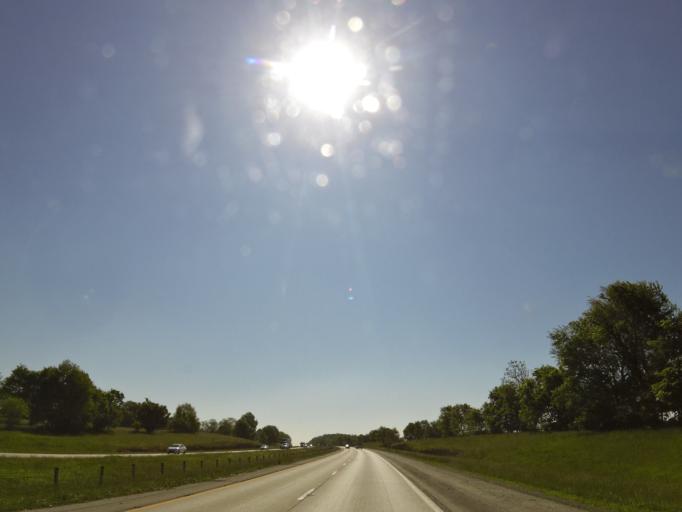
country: US
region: Kentucky
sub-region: Woodford County
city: Midway
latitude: 38.1636
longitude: -84.7407
